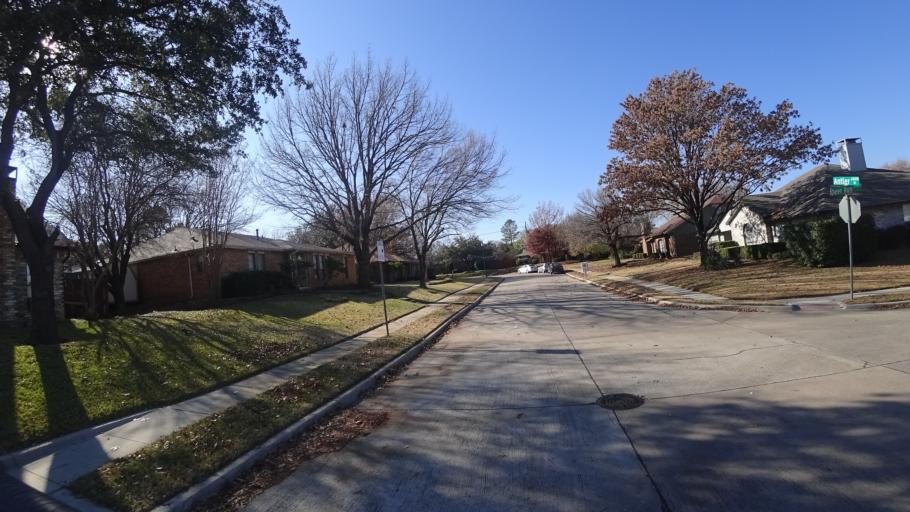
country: US
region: Texas
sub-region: Denton County
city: Lewisville
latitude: 33.0083
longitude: -96.9980
